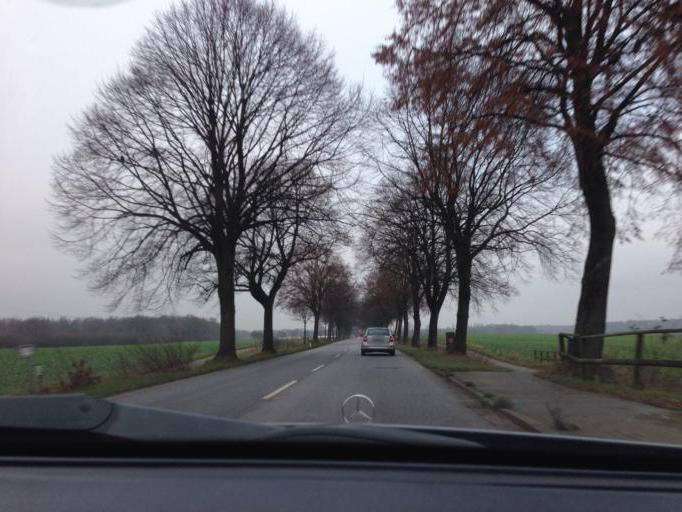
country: DE
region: Schleswig-Holstein
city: Stapelfeld
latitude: 53.6379
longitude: 10.1926
